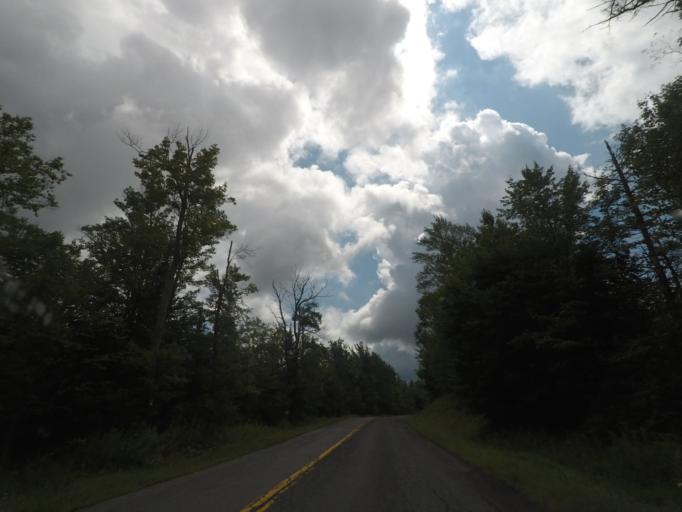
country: US
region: New York
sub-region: Rensselaer County
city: Poestenkill
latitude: 42.6865
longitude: -73.4330
